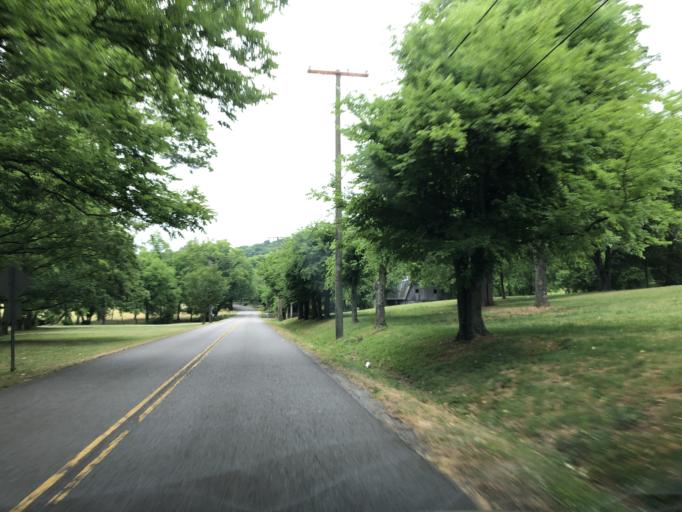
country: US
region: Tennessee
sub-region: Davidson County
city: Goodlettsville
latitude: 36.2843
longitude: -86.7563
